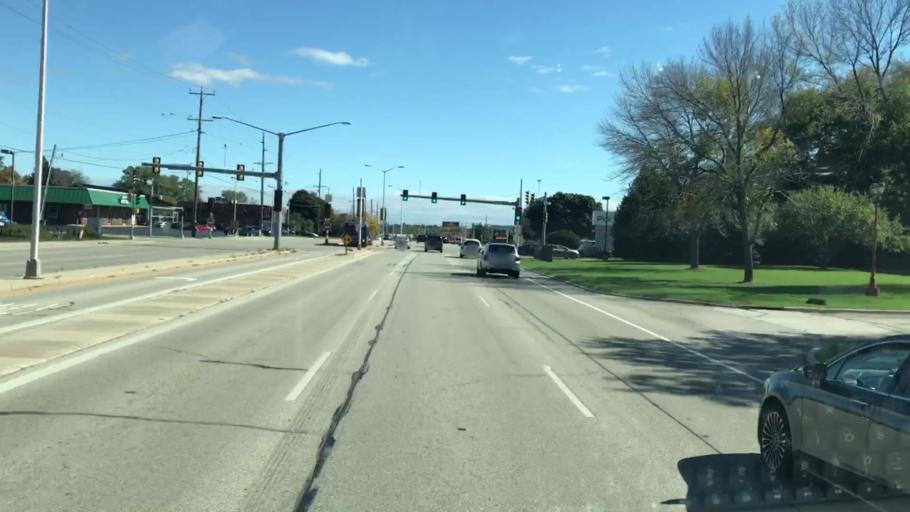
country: US
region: Wisconsin
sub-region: Waukesha County
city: Butler
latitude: 43.0891
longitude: -88.0723
